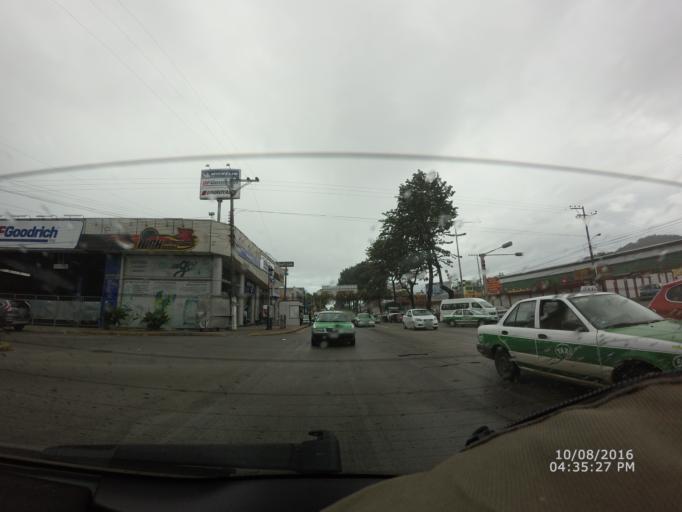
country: MX
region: Veracruz
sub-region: Xalapa
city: Xalapa de Enriquez
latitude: 19.5601
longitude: -96.9226
